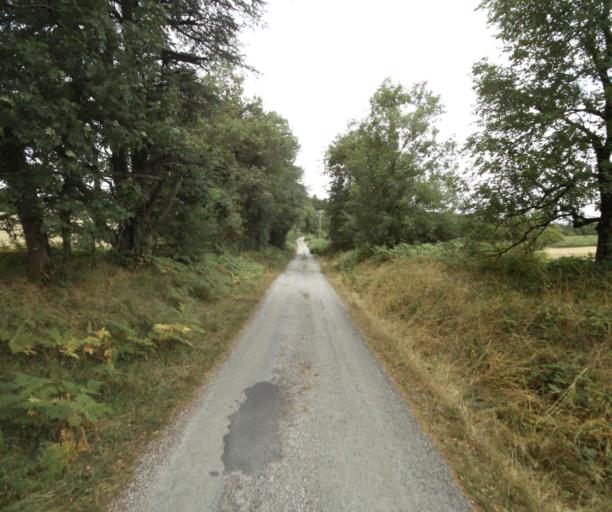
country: FR
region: Midi-Pyrenees
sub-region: Departement du Tarn
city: Soreze
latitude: 43.4249
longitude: 2.0945
